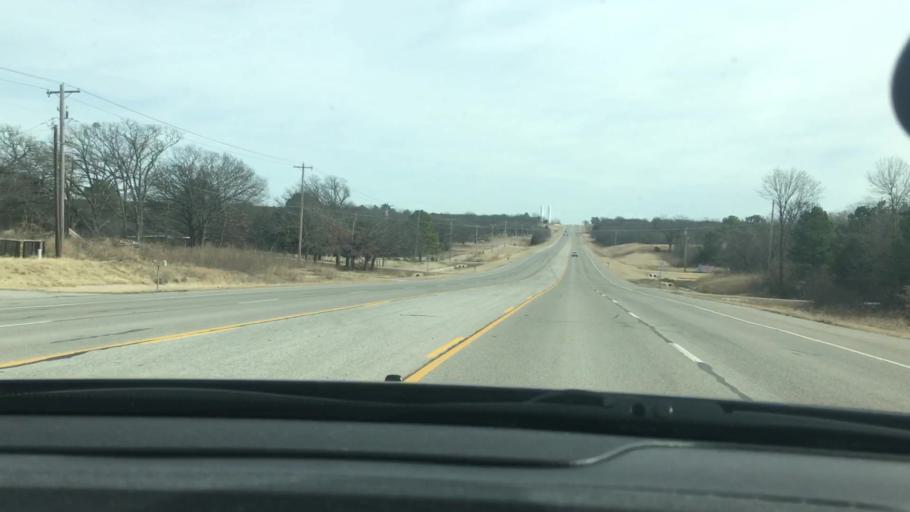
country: US
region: Oklahoma
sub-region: Carter County
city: Dickson
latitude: 34.1871
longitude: -97.0160
